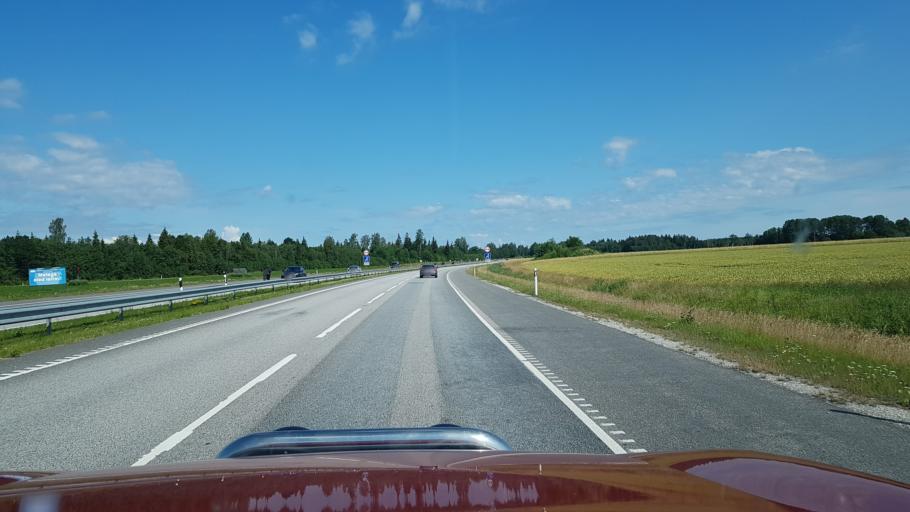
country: EE
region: Jaervamaa
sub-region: Paide linn
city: Paide
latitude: 58.9320
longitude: 25.6107
